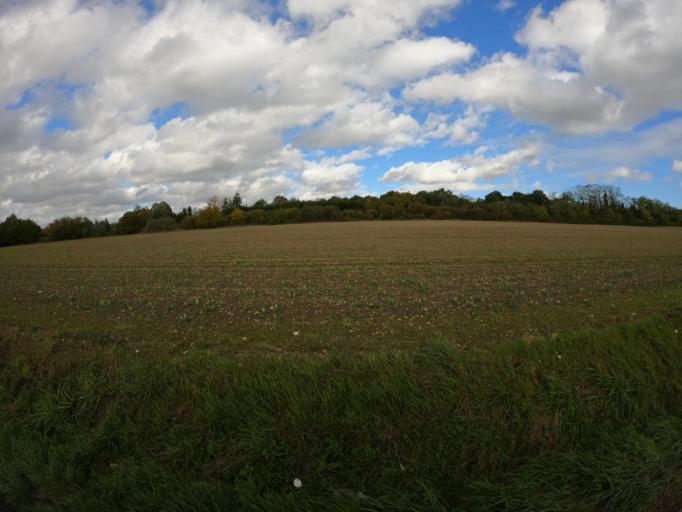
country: FR
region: Ile-de-France
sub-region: Departement de Seine-et-Marne
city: Chalifert
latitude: 48.9000
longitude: 2.7838
